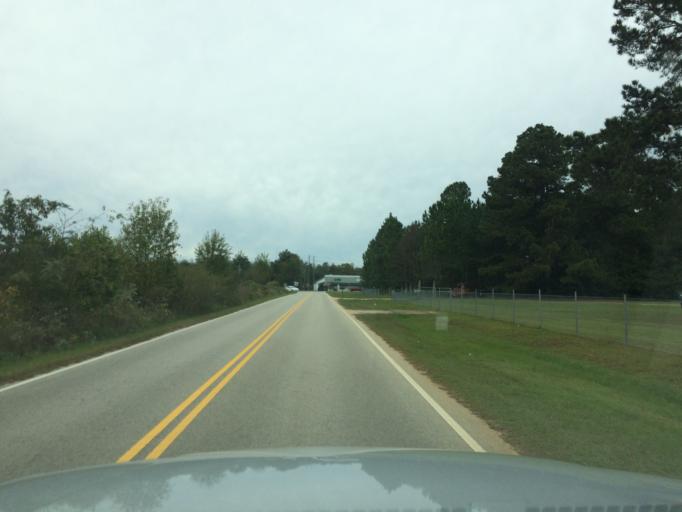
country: US
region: South Carolina
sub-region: Aiken County
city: New Ellenton
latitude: 33.4630
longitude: -81.6850
